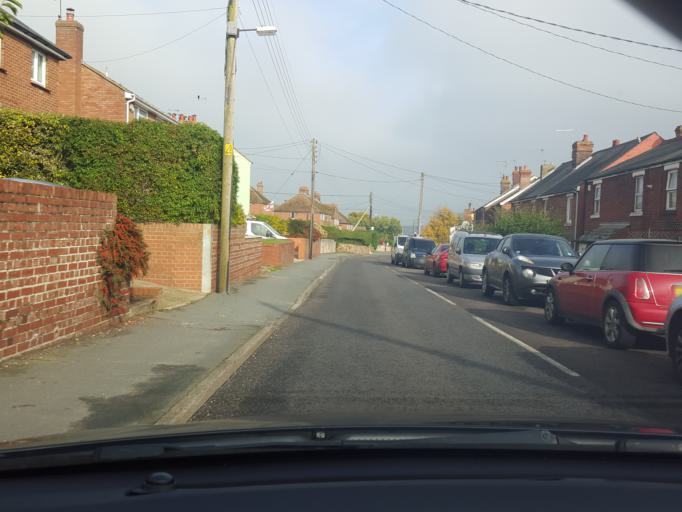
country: GB
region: England
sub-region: Essex
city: Manningtree
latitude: 51.9421
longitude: 1.0581
